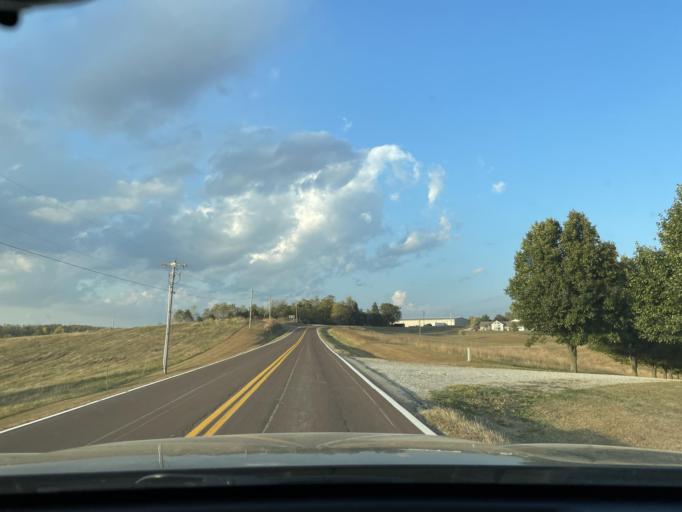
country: US
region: Missouri
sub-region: Andrew County
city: Savannah
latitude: 39.9137
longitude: -94.8763
